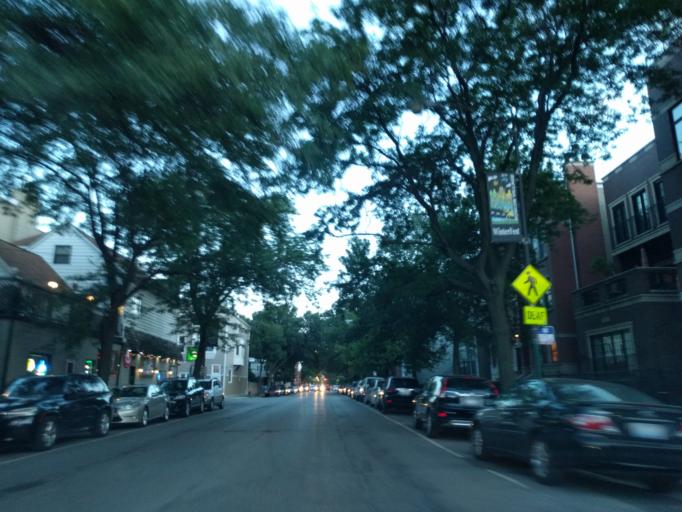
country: US
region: Illinois
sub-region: Cook County
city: Lincolnwood
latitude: 41.9428
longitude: -87.6785
